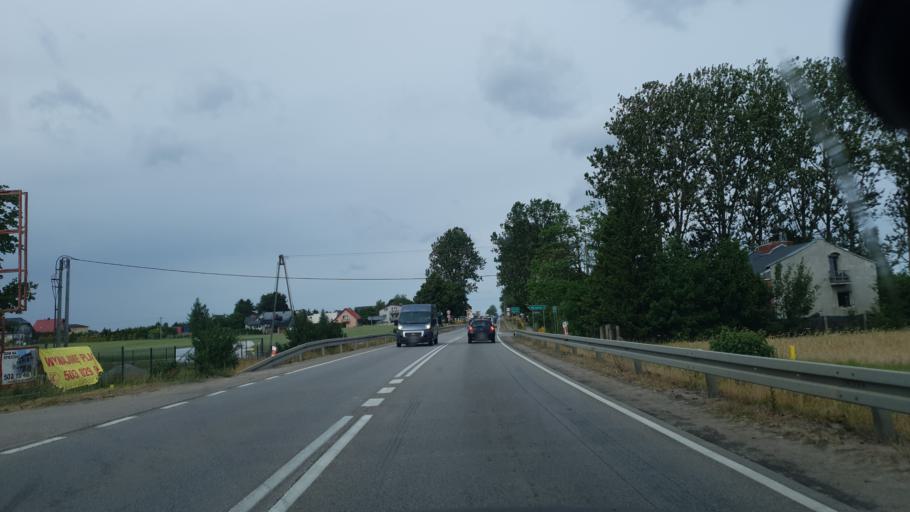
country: PL
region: Pomeranian Voivodeship
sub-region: Powiat kartuski
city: Banino
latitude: 54.4154
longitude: 18.3746
